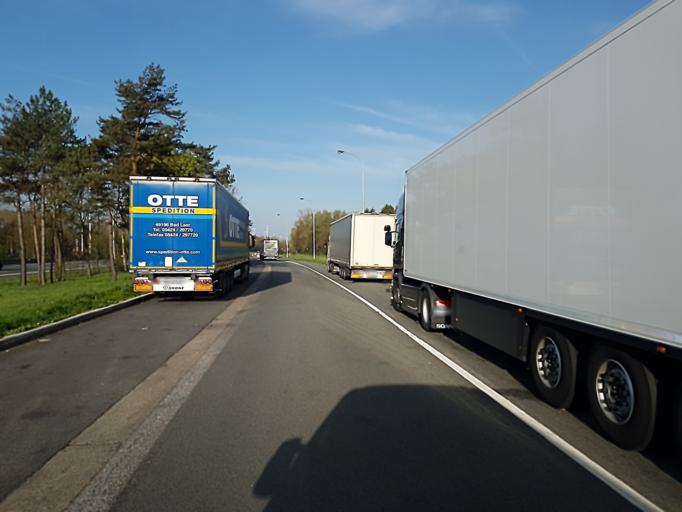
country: BE
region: Flanders
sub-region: Provincie Antwerpen
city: Vorselaar
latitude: 51.2444
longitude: 4.7565
